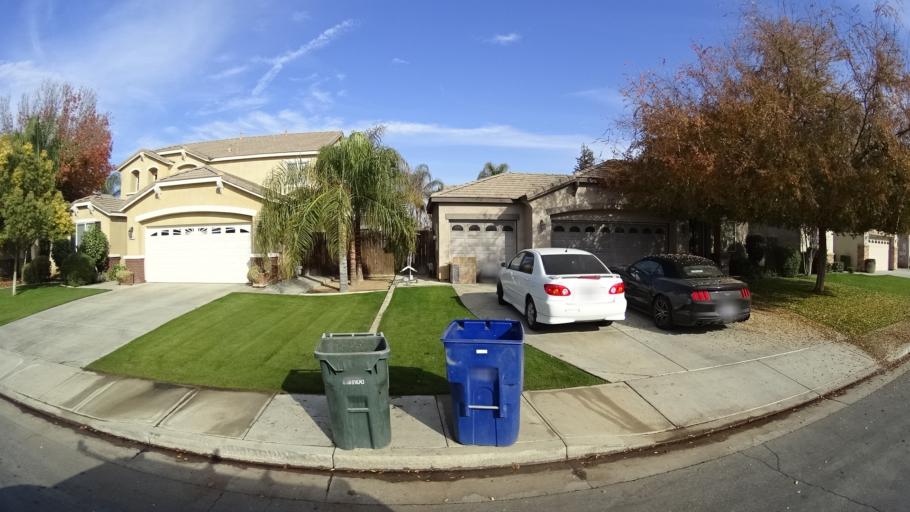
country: US
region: California
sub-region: Kern County
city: Rosedale
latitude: 35.4110
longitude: -119.1380
